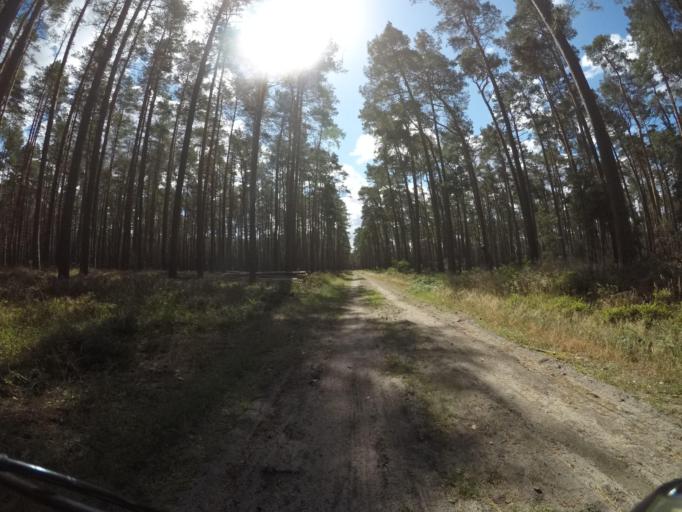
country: DE
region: Lower Saxony
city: Hitzacker
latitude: 53.2155
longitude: 11.0478
